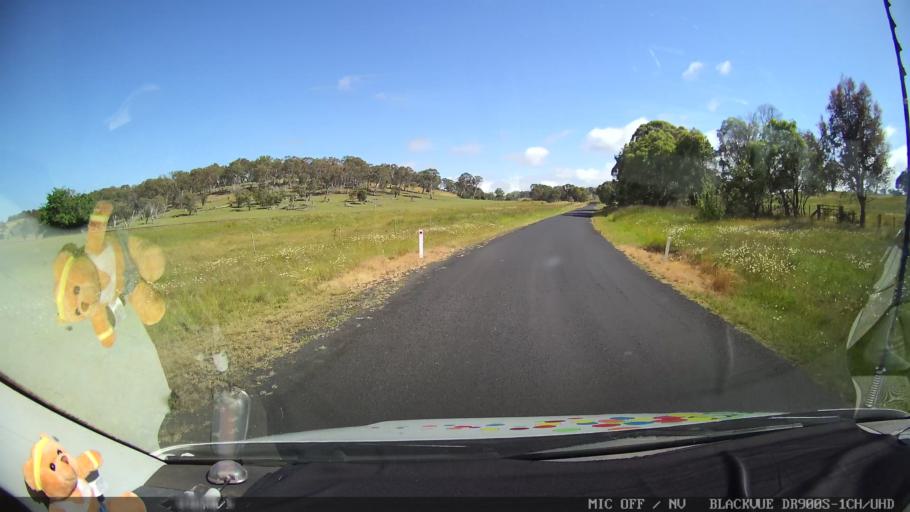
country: AU
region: New South Wales
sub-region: Guyra
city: Guyra
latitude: -30.1228
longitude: 151.6863
